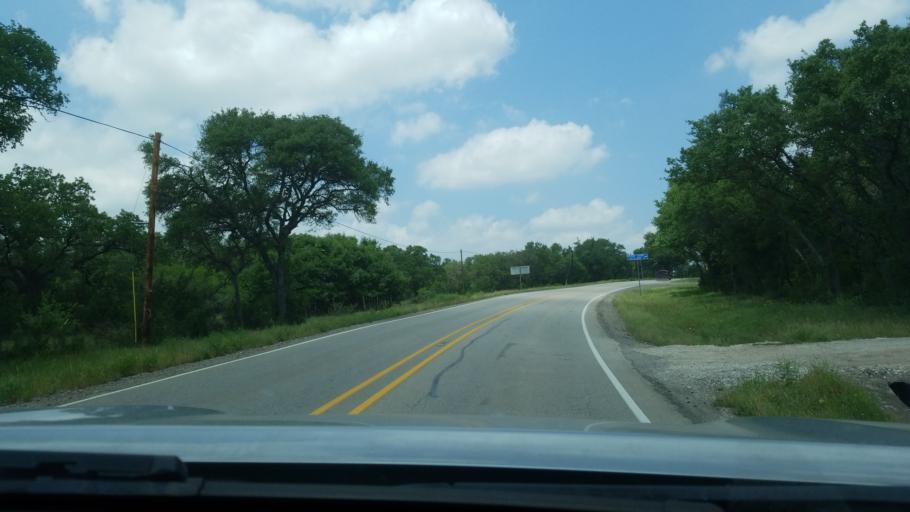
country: US
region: Texas
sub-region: Hays County
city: Dripping Springs
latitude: 30.1453
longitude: -98.0511
